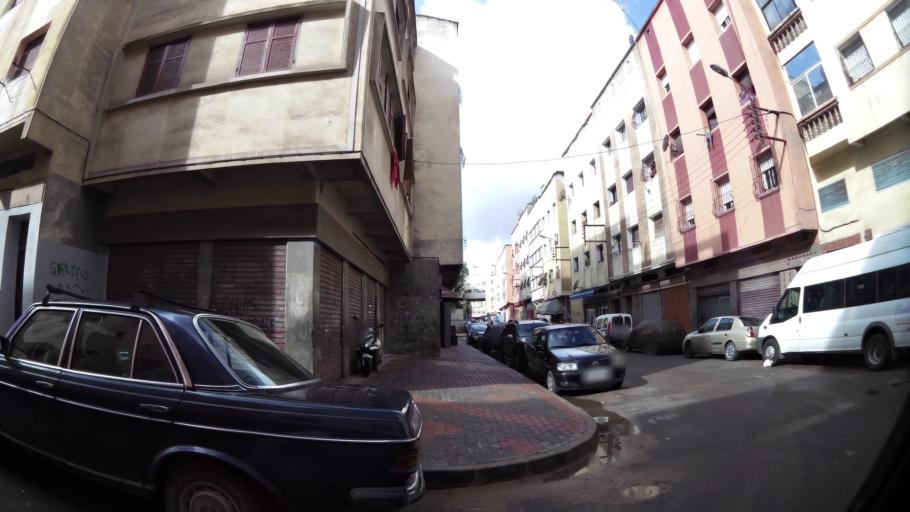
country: MA
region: Grand Casablanca
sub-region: Casablanca
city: Casablanca
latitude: 33.5709
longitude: -7.5801
